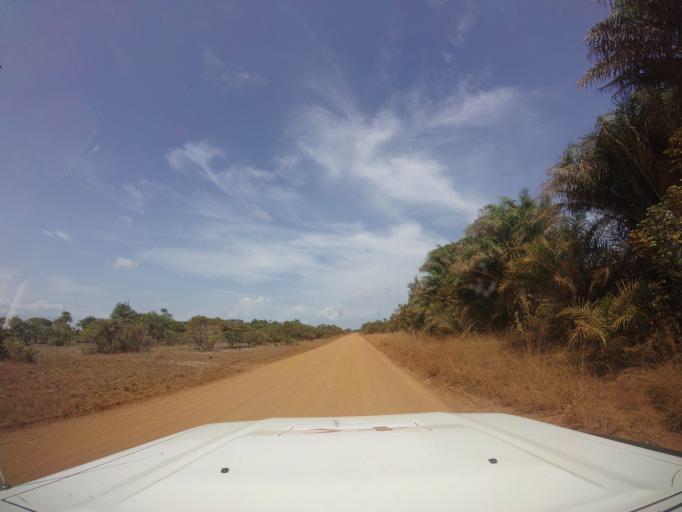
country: LR
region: Grand Cape Mount
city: Robertsport
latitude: 6.7044
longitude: -11.3051
